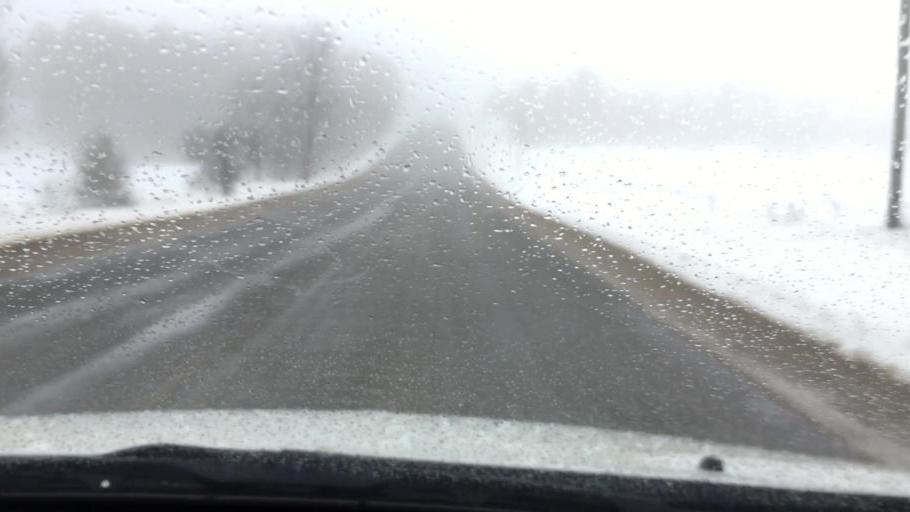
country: US
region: Michigan
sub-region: Charlevoix County
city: East Jordan
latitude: 45.1325
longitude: -85.1773
